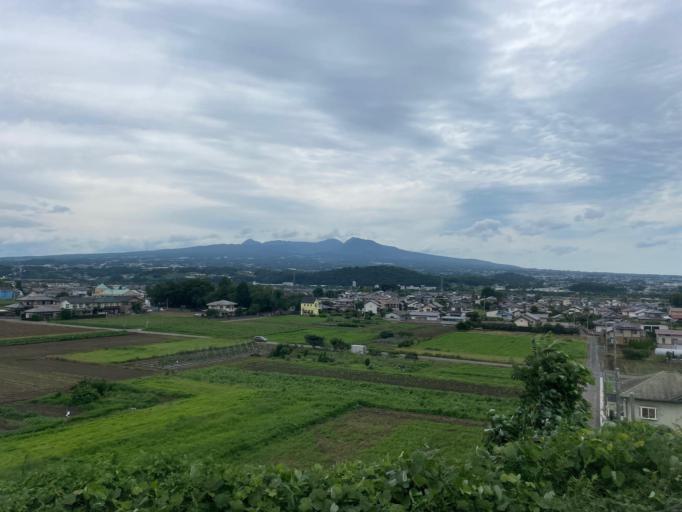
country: JP
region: Gunma
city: Kanekomachi
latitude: 36.4433
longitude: 139.0248
